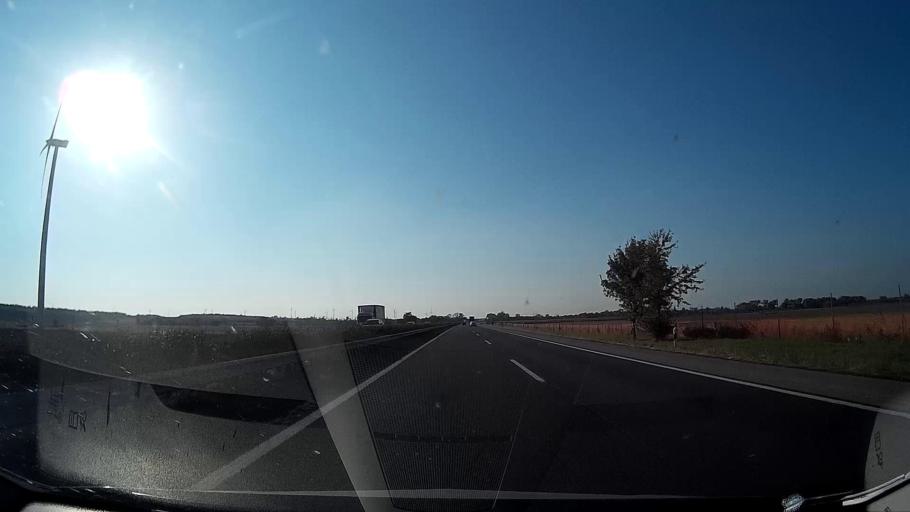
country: HU
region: Komarom-Esztergom
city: Babolna
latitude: 47.6793
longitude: 17.9328
